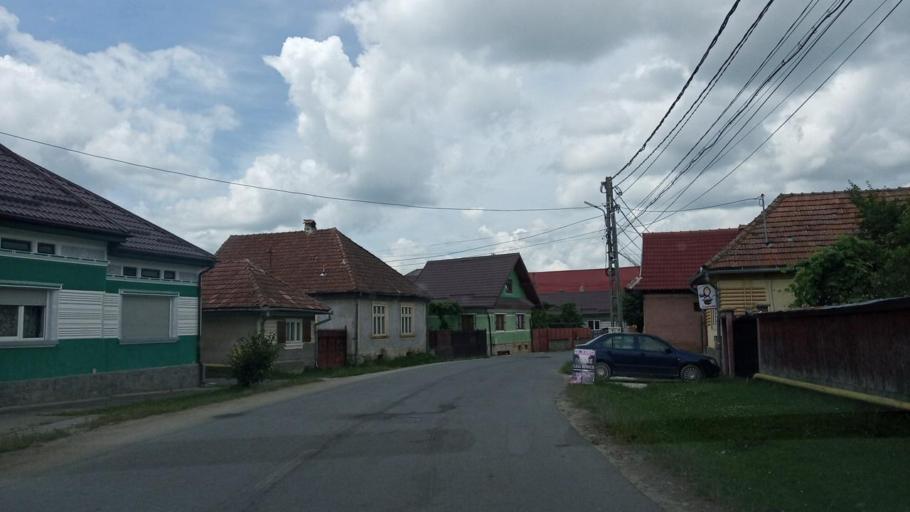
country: RO
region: Sibiu
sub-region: Comuna Cartisoara
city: Cartisoara
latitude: 45.7271
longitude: 24.5806
